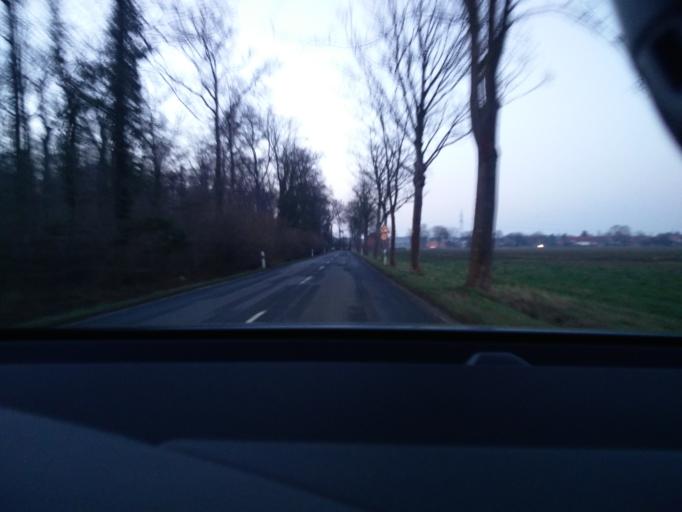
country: DE
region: Lower Saxony
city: Laatzen
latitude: 52.3207
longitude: 9.8528
